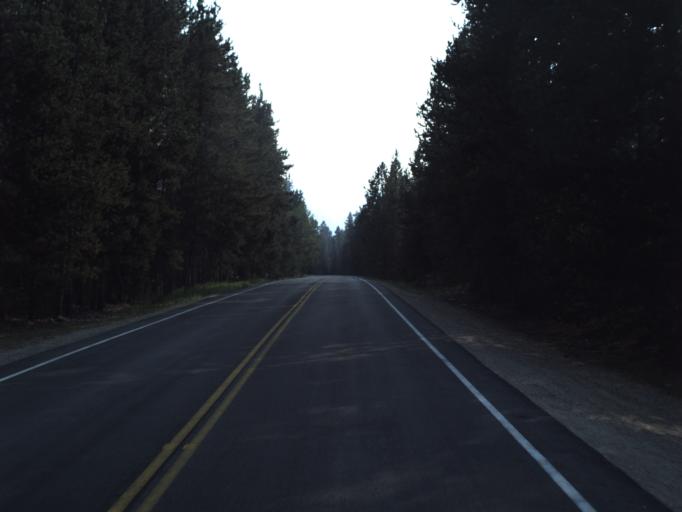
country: US
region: Utah
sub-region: Summit County
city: Francis
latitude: 40.5883
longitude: -111.0176
